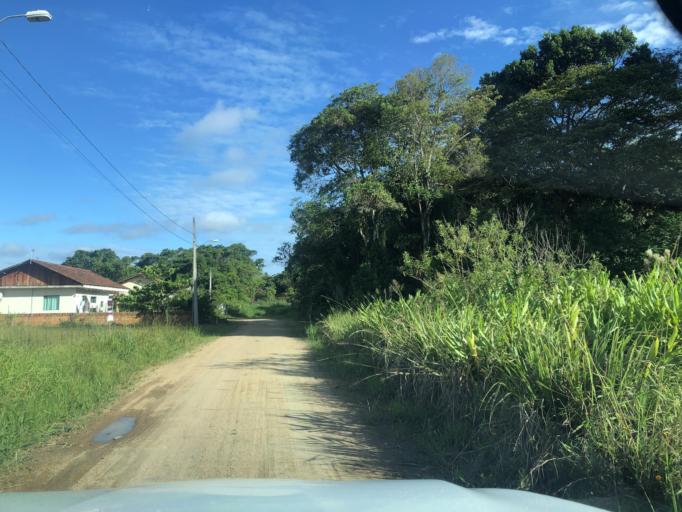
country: BR
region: Santa Catarina
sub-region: Sao Francisco Do Sul
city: Sao Francisco do Sul
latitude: -26.2121
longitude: -48.5366
